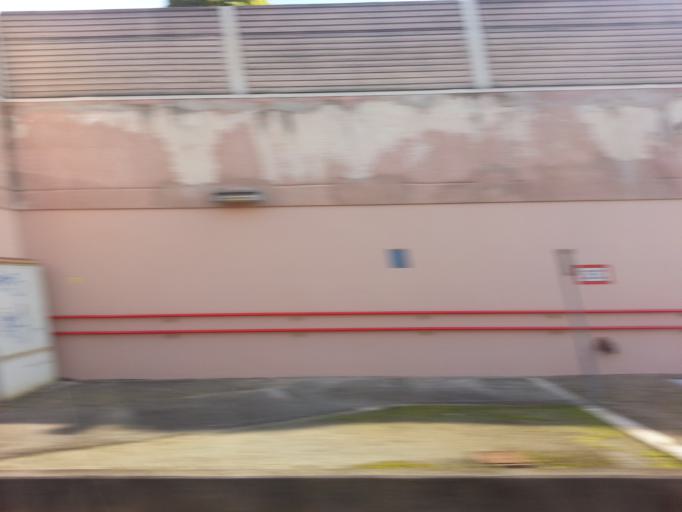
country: NL
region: North Brabant
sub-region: Gemeente Best
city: Best
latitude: 51.5113
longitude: 5.3880
